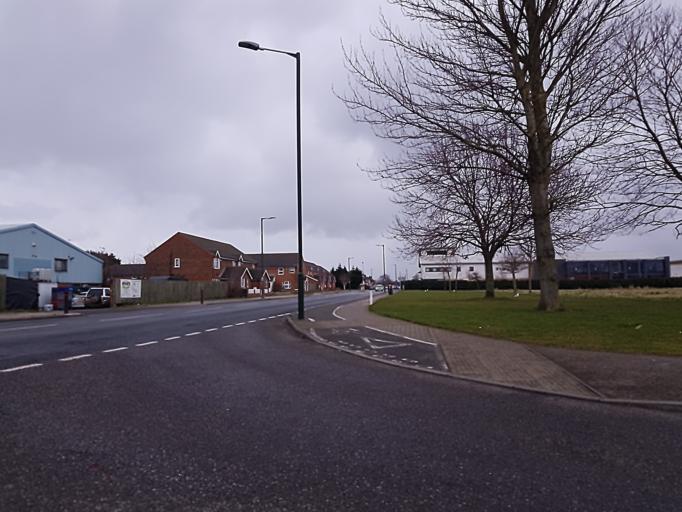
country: GB
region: England
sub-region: North East Lincolnshire
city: Grimbsy
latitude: 53.5687
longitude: -0.1112
